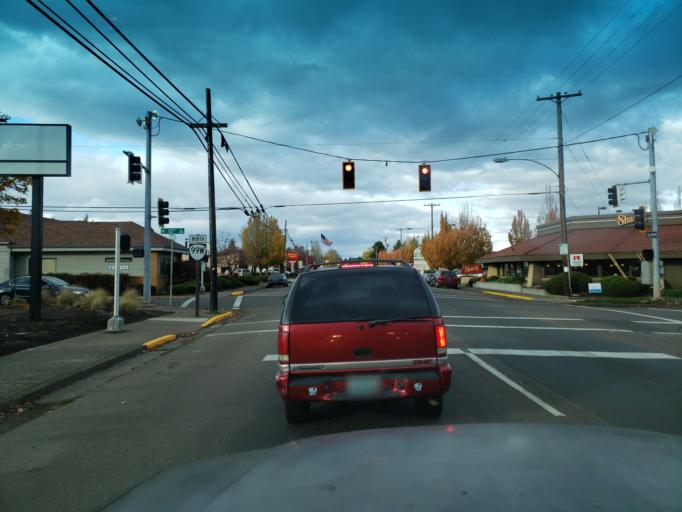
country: US
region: Oregon
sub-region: Yamhill County
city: McMinnville
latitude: 45.2163
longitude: -123.1980
